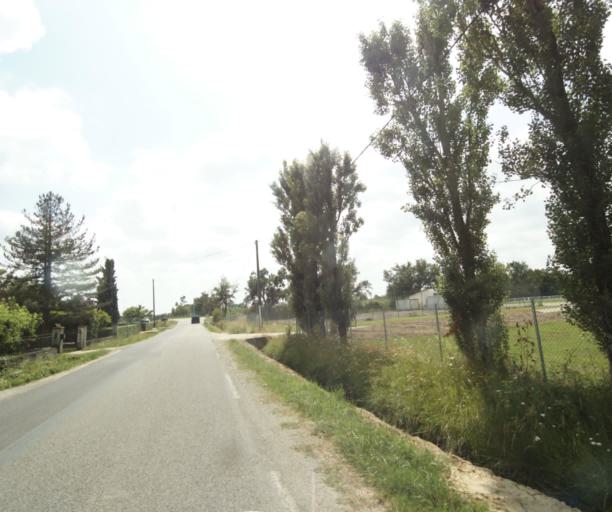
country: FR
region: Midi-Pyrenees
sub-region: Departement du Tarn-et-Garonne
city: Montauban
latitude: 44.0455
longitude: 1.3805
